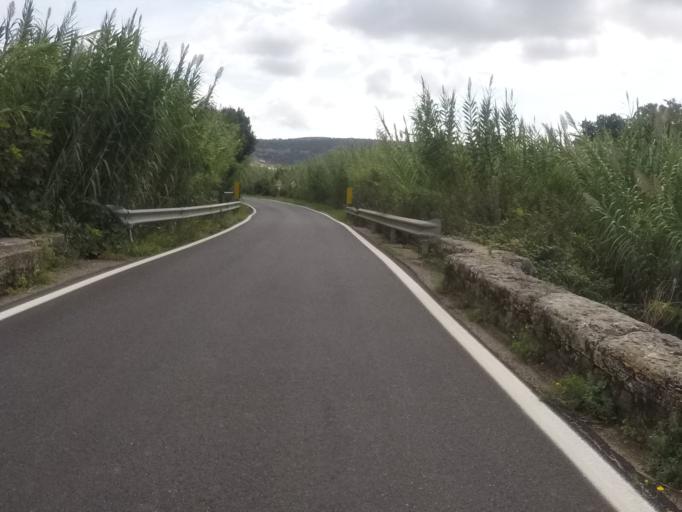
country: IT
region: Sardinia
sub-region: Provincia di Oristano
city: Bauladu
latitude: 40.0232
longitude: 8.6654
